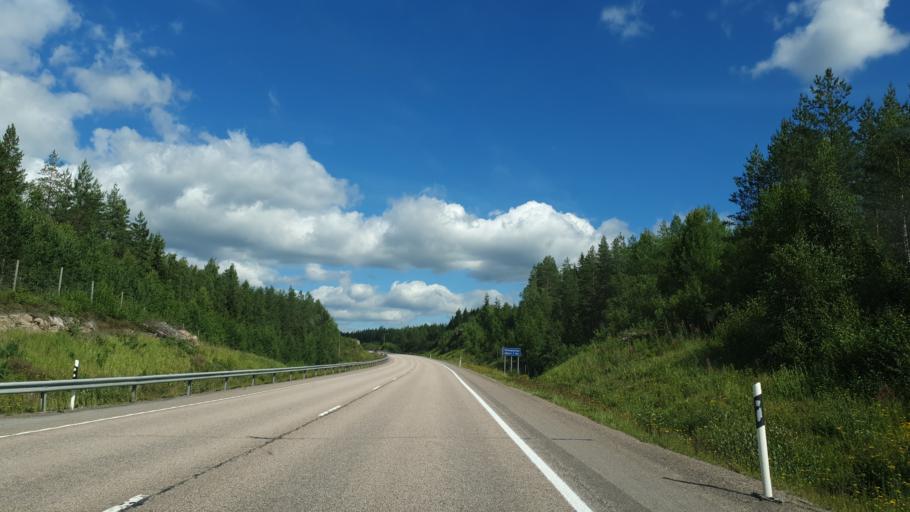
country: FI
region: Central Finland
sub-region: Jaemsae
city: Jaemsae
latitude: 61.8007
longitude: 24.9616
